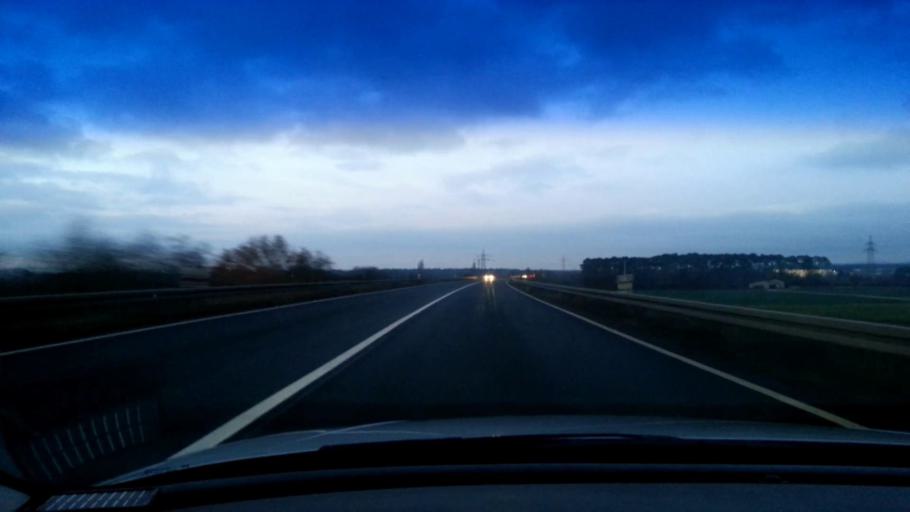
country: DE
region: Bavaria
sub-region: Upper Franconia
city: Pettstadt
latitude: 49.8368
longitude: 10.9491
